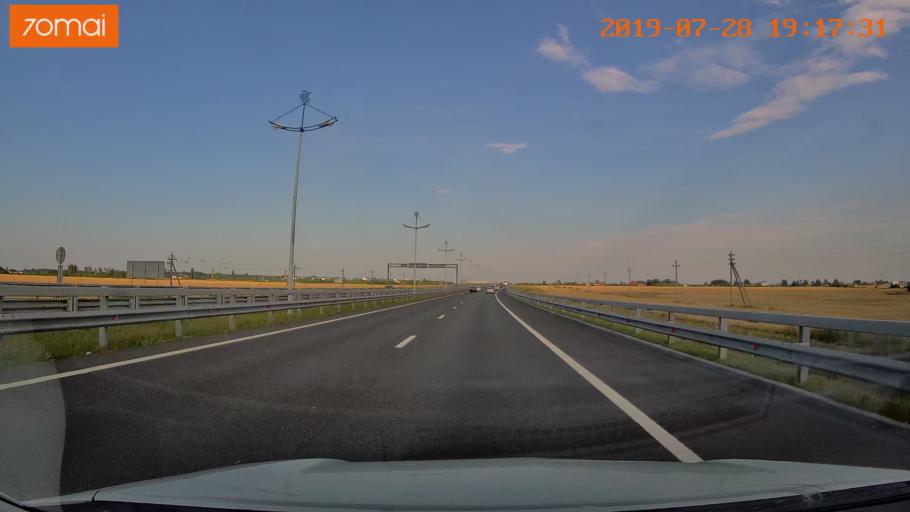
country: RU
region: Kaliningrad
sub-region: Zelenogradskiy Rayon
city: Zelenogradsk
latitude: 54.9220
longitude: 20.4053
